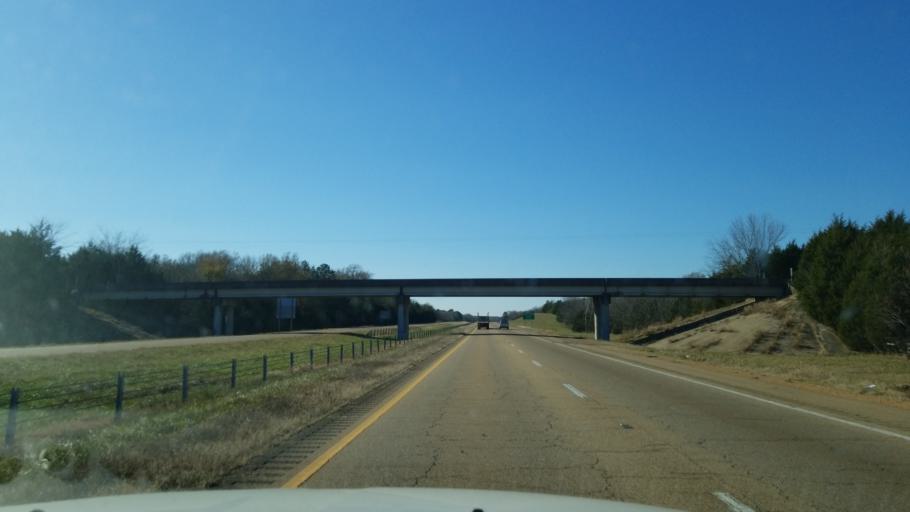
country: US
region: Mississippi
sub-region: Clay County
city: West Point
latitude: 33.4847
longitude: -88.6789
